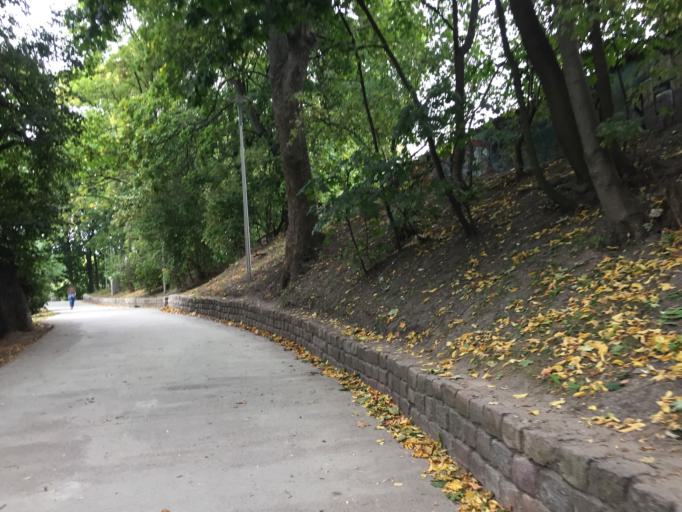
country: RU
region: Kaliningrad
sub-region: Gorod Kaliningrad
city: Kaliningrad
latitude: 54.7159
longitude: 20.5195
